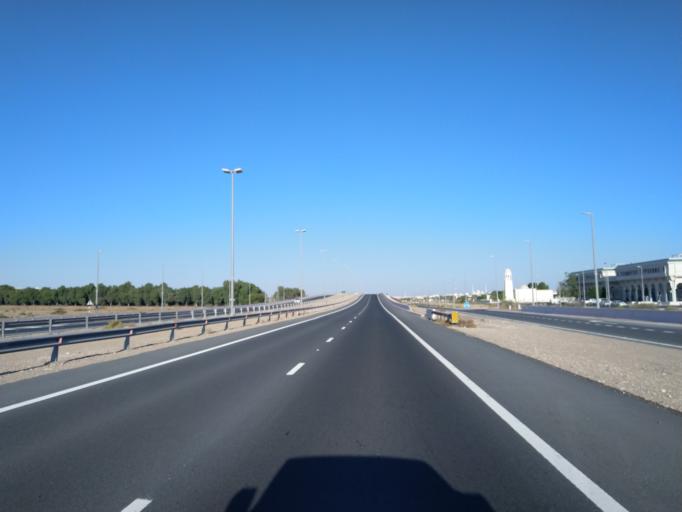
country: OM
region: Al Buraimi
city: Al Buraymi
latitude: 24.5118
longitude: 55.4824
